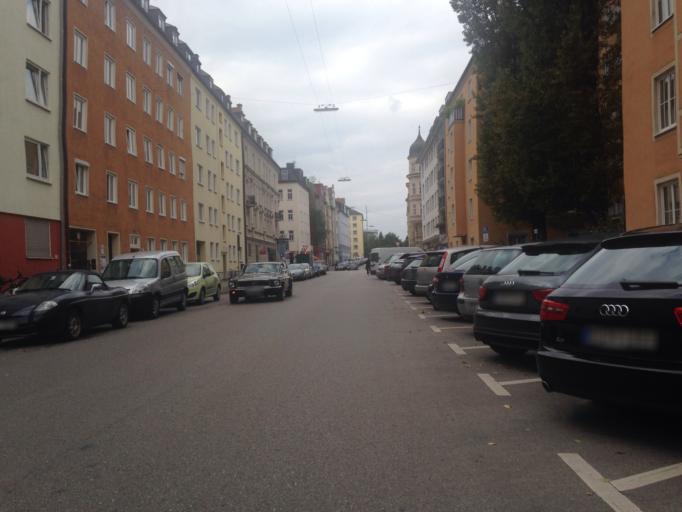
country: DE
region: Bavaria
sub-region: Upper Bavaria
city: Munich
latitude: 48.1571
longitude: 11.5635
